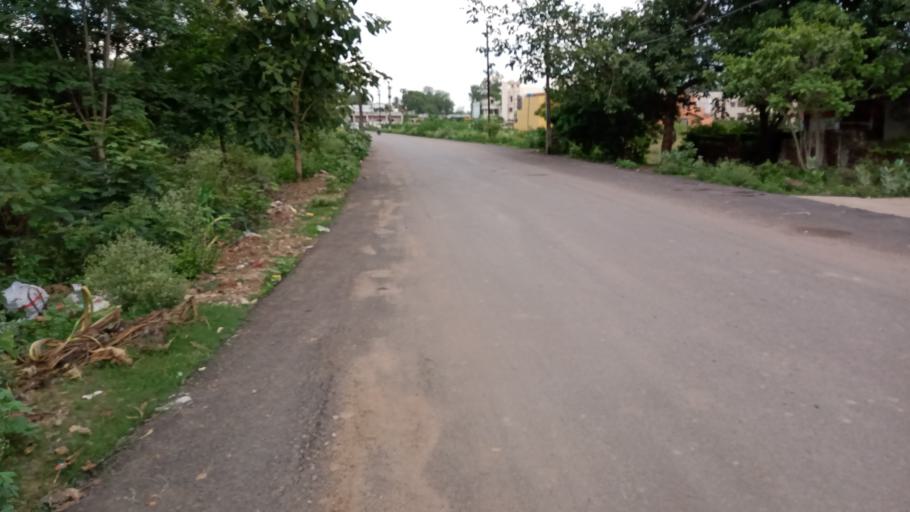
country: IN
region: Chhattisgarh
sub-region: Bastar
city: Jagdalpur
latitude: 19.0935
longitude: 81.9935
